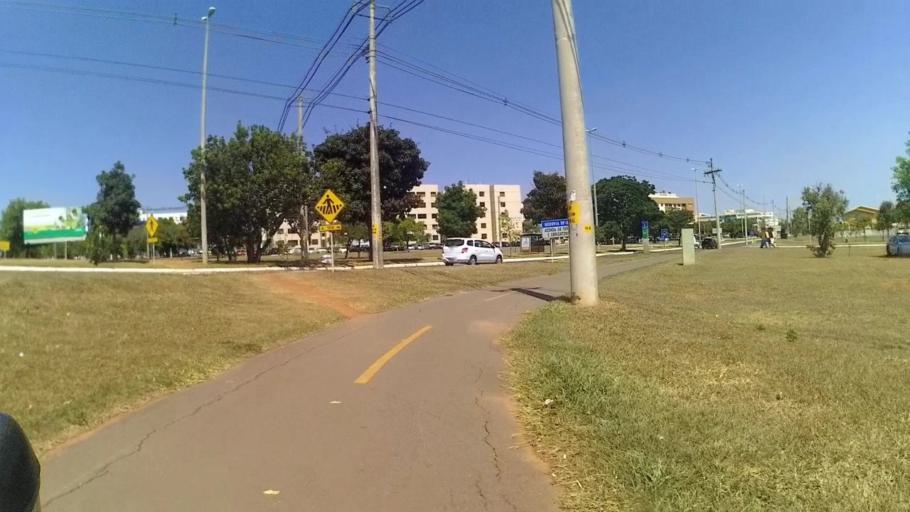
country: BR
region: Federal District
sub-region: Brasilia
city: Brasilia
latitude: -15.7155
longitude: -47.8816
